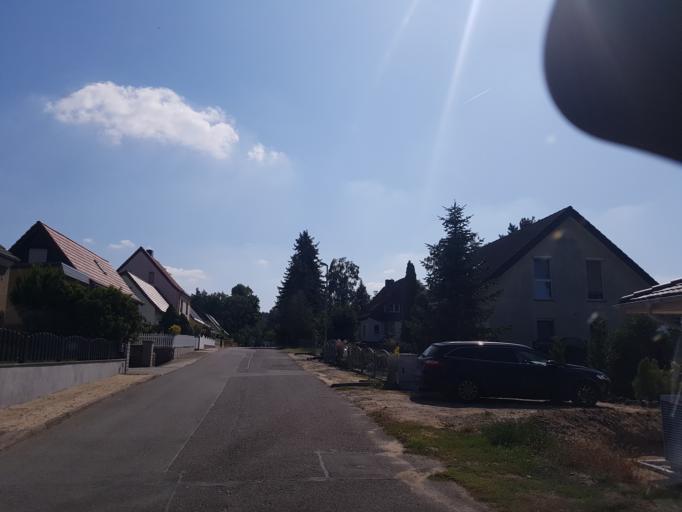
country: DE
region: Brandenburg
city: Elsterwerda
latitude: 51.5003
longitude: 13.4977
